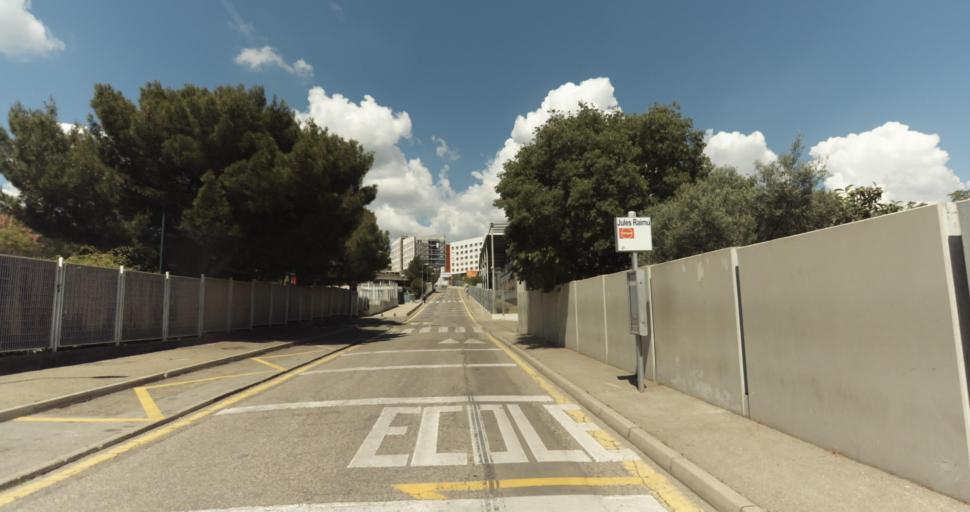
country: FR
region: Languedoc-Roussillon
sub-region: Departement du Gard
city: Nimes
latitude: 43.8187
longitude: 4.3294
